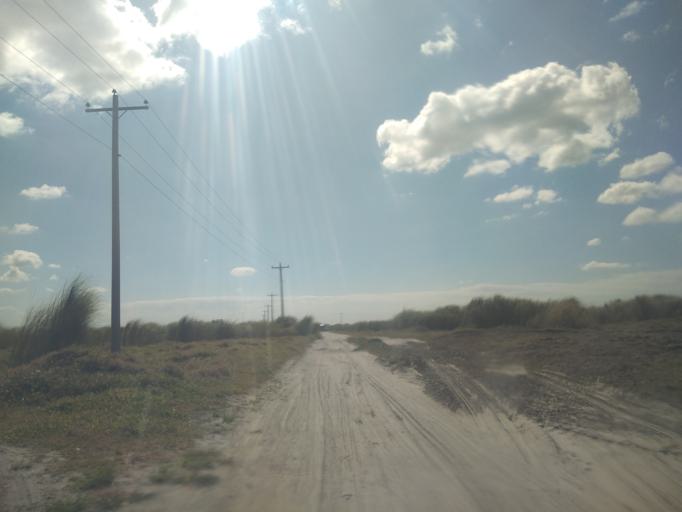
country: PH
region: Central Luzon
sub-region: Province of Pampanga
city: Balas
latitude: 15.0624
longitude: 120.5940
